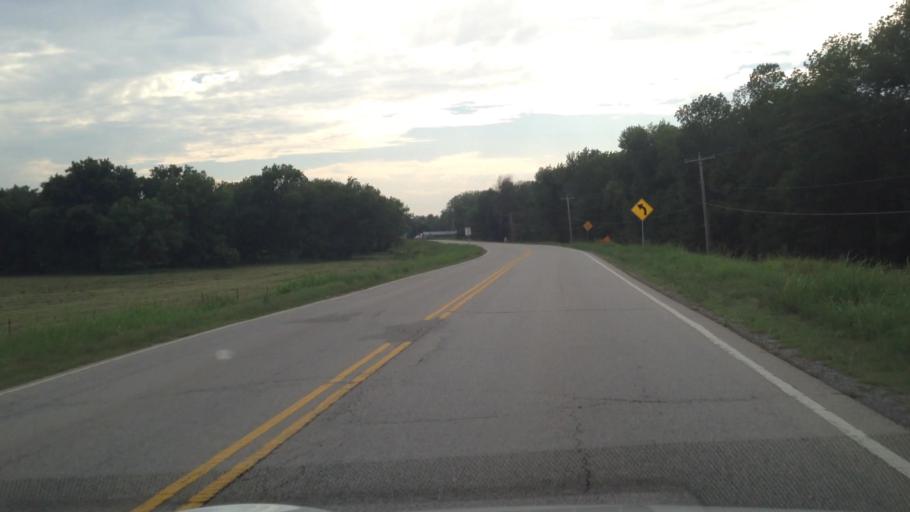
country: US
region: Oklahoma
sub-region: Ottawa County
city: Afton
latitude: 36.6984
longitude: -94.9527
